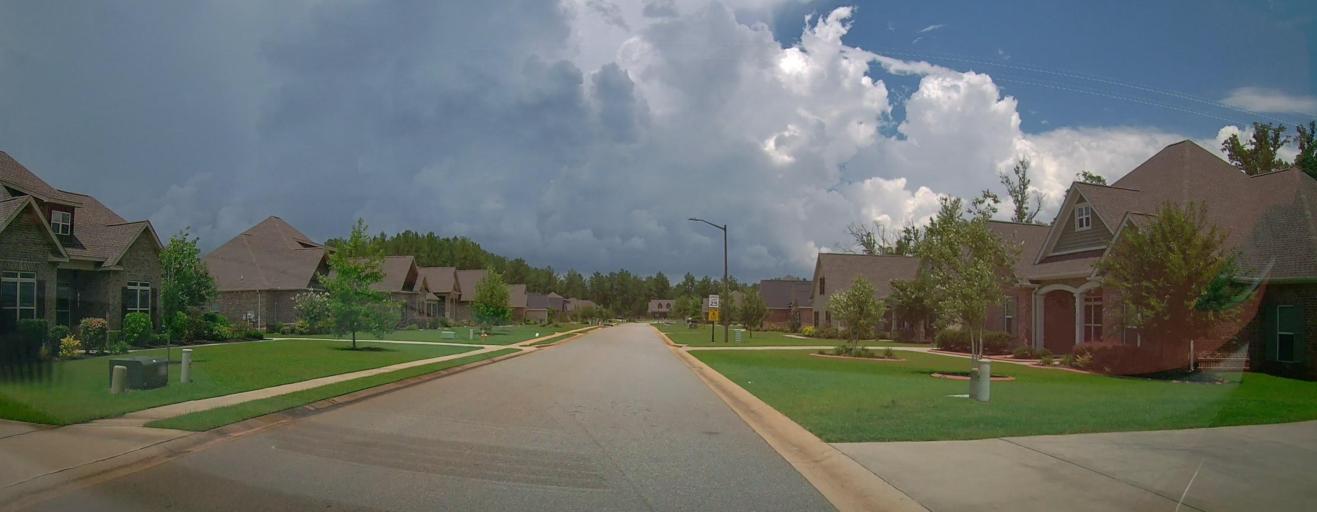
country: US
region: Georgia
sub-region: Houston County
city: Robins Air Force Base
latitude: 32.5122
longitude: -83.6353
